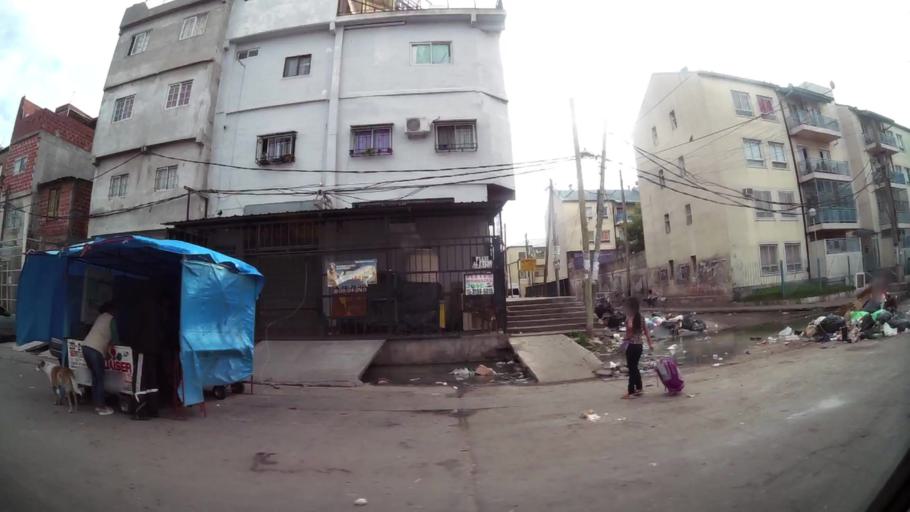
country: AR
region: Buenos Aires F.D.
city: Villa Lugano
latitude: -34.6470
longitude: -58.4440
